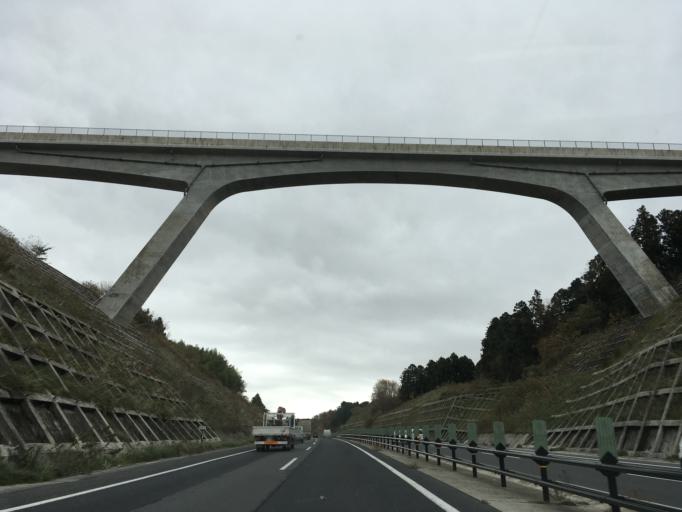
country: JP
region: Miyagi
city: Yamoto
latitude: 38.5452
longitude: 141.2728
